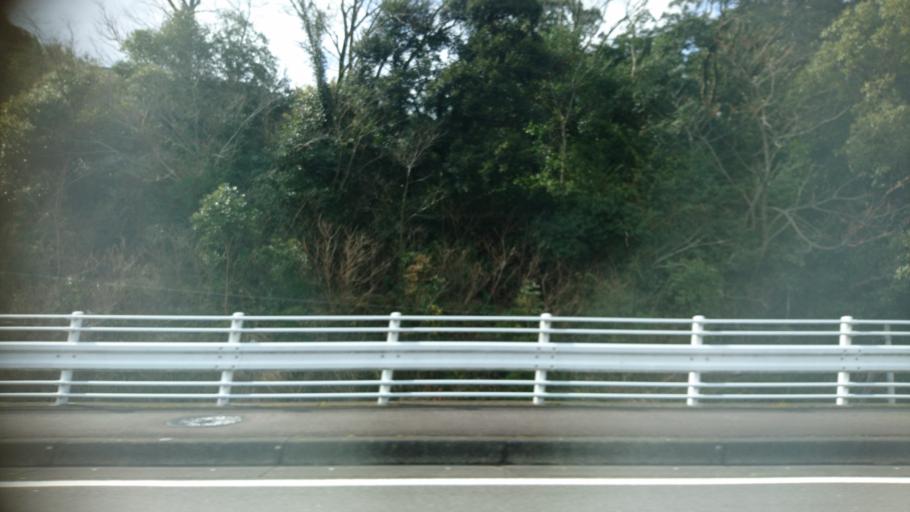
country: JP
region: Kagoshima
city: Satsumasendai
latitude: 31.8074
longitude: 130.3073
